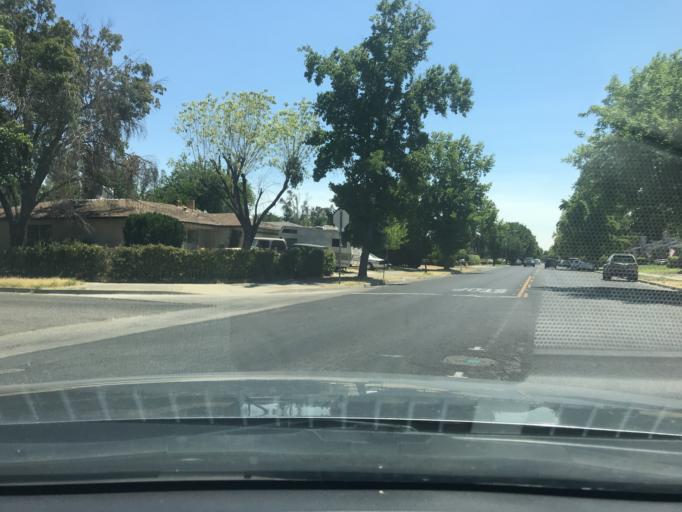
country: US
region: California
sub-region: Merced County
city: Merced
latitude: 37.3234
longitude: -120.4930
